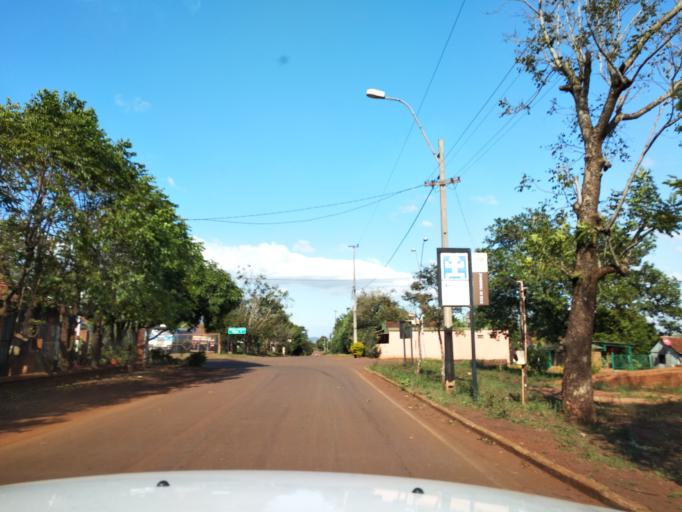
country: PY
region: Itapua
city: Hohenau
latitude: -27.0585
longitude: -55.7451
